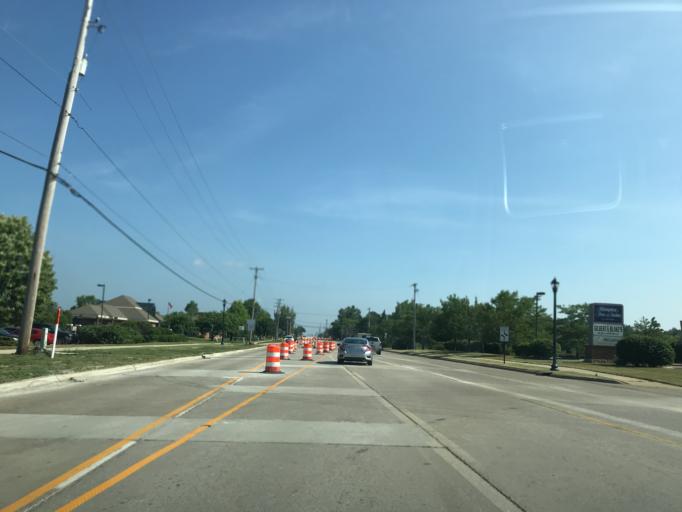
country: US
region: Michigan
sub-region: Ingham County
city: Okemos
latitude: 42.6841
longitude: -84.4324
